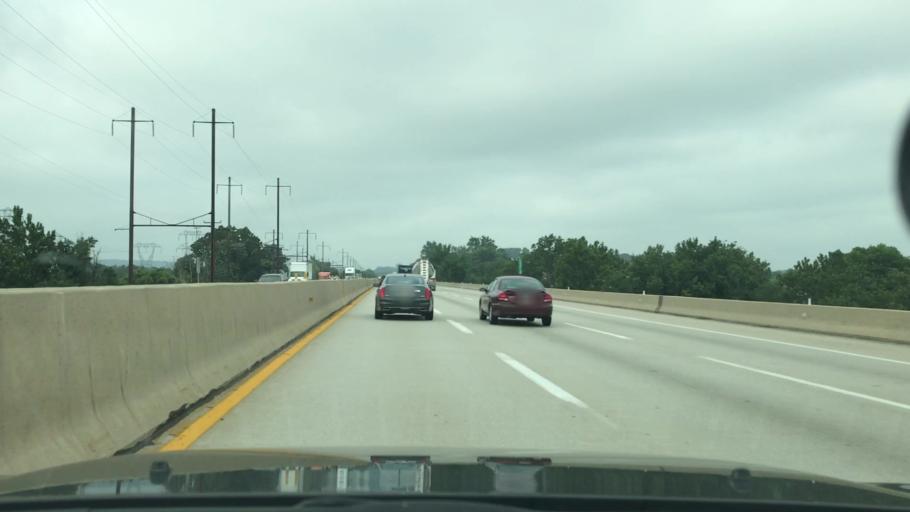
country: US
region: Pennsylvania
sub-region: Montgomery County
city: Bridgeport
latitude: 40.1034
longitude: -75.3244
